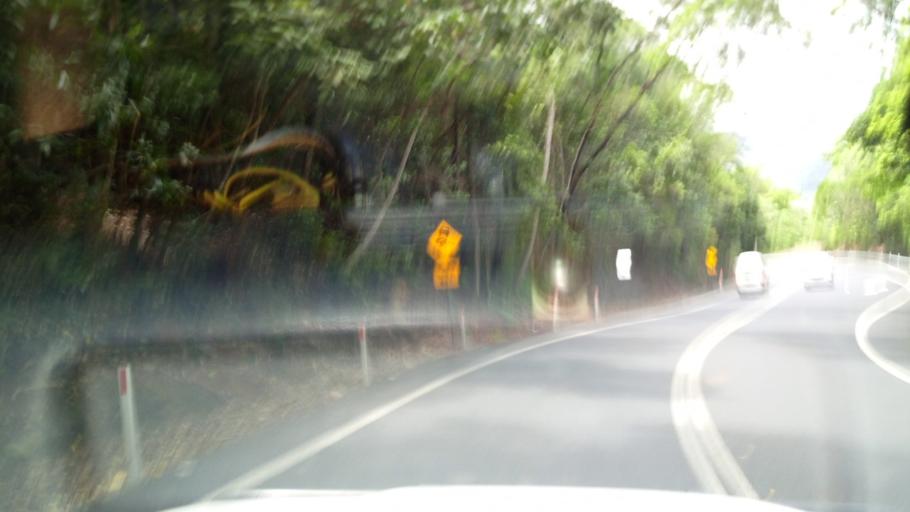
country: AU
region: Queensland
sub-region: Cairns
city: Redlynch
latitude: -16.8497
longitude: 145.6856
